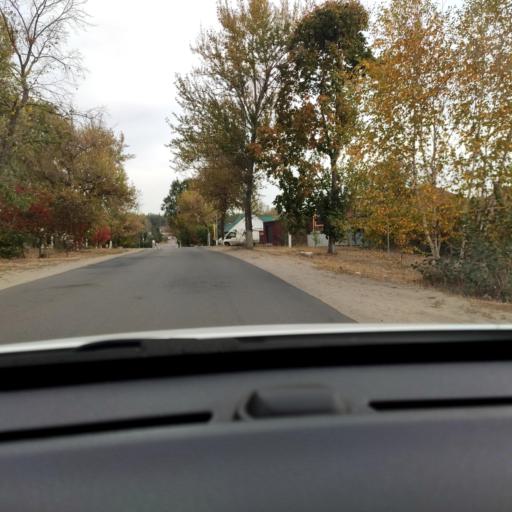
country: RU
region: Voronezj
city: Somovo
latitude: 51.6902
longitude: 39.3186
